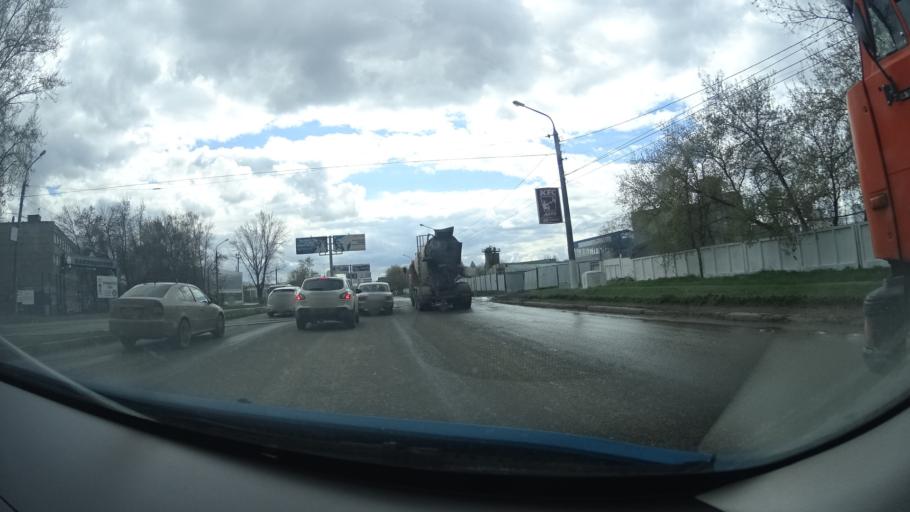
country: RU
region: Bashkortostan
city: Ufa
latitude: 54.8044
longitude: 56.0821
